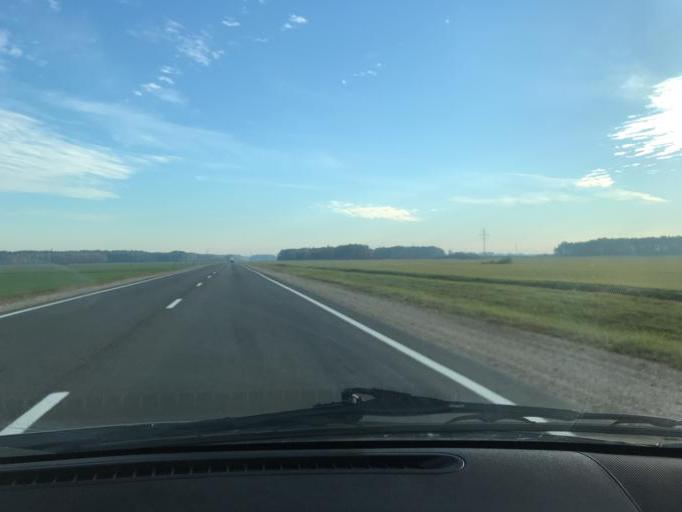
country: BY
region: Brest
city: Drahichyn
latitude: 52.2061
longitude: 25.0631
